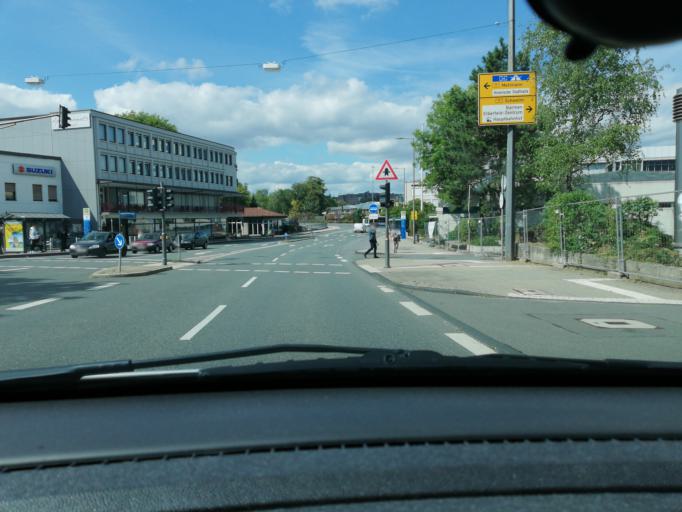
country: DE
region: North Rhine-Westphalia
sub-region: Regierungsbezirk Dusseldorf
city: Wuppertal
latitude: 51.2524
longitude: 7.1464
